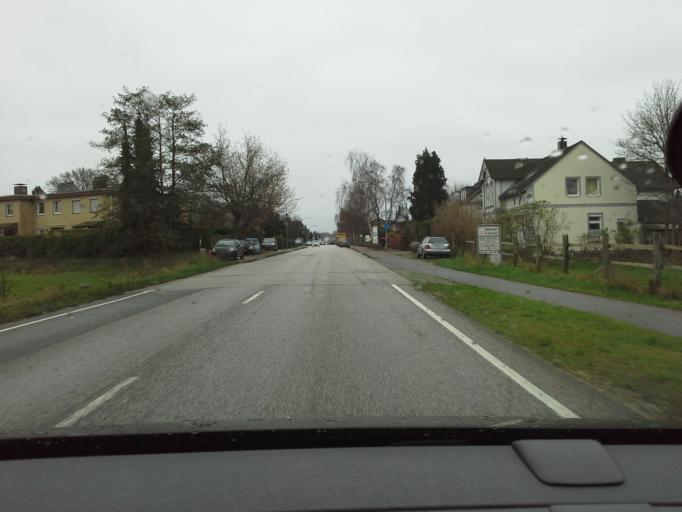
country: DE
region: Schleswig-Holstein
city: Quickborn
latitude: 53.7379
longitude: 9.8915
